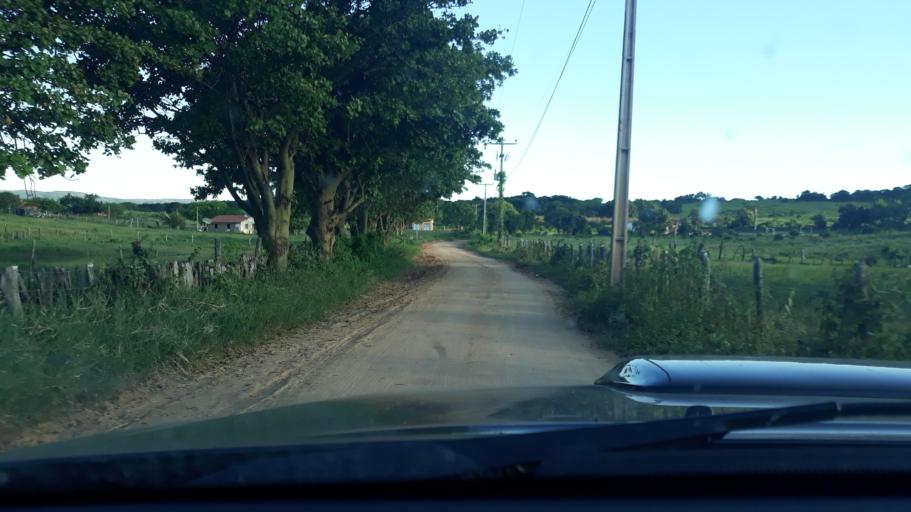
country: BR
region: Bahia
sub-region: Riacho De Santana
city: Riacho de Santana
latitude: -13.8317
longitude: -42.7301
